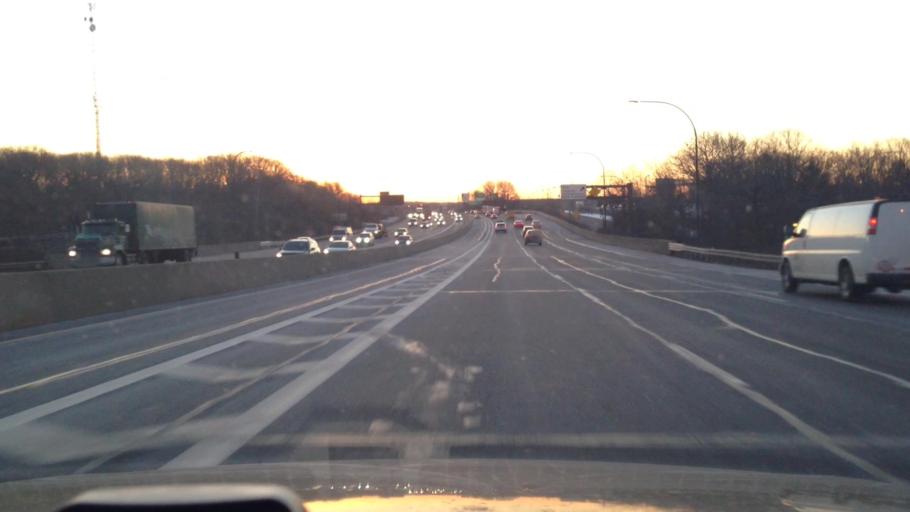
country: US
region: New York
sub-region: Nassau County
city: Plainview
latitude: 40.7898
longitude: -73.4567
